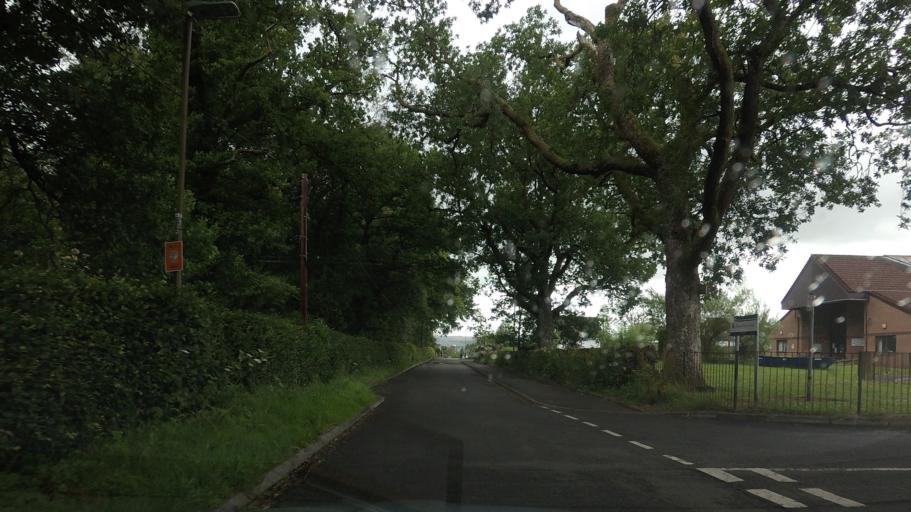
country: GB
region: Scotland
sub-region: Stirling
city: Killearn
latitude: 56.0698
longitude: -4.4511
